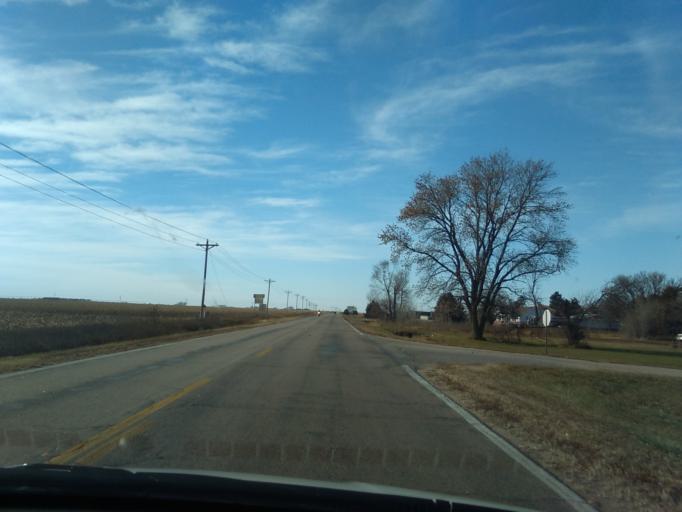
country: US
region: Nebraska
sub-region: Clay County
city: Harvard
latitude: 40.6115
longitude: -98.0983
